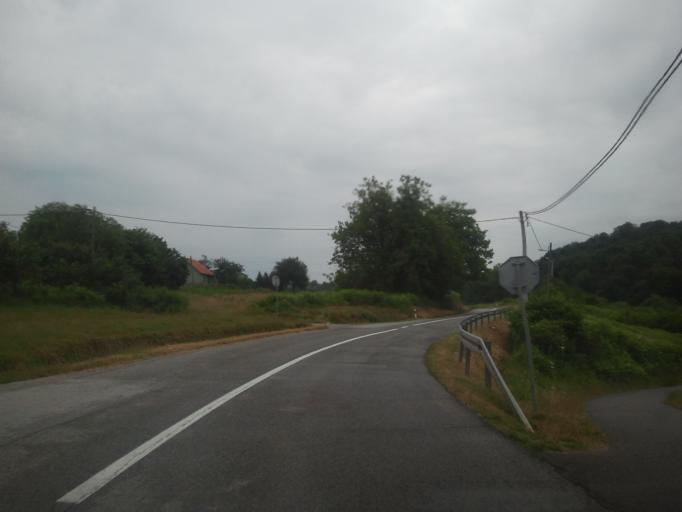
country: HR
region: Karlovacka
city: Vojnic
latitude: 45.3391
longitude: 15.7302
